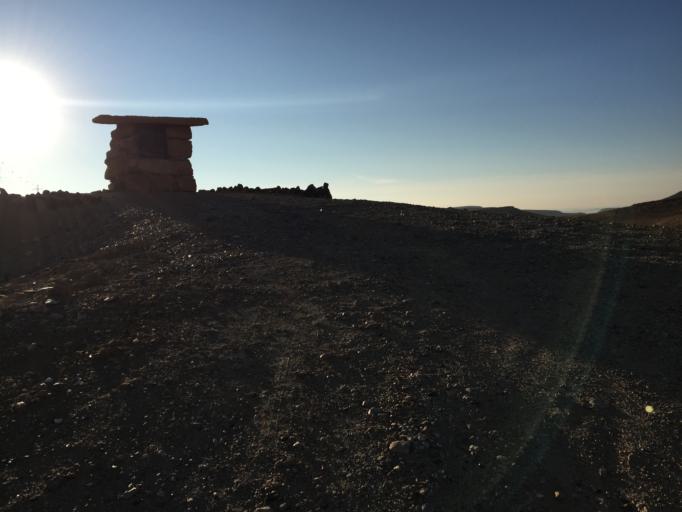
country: IL
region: Southern District
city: Mitzpe Ramon
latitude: 30.5287
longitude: 34.9204
